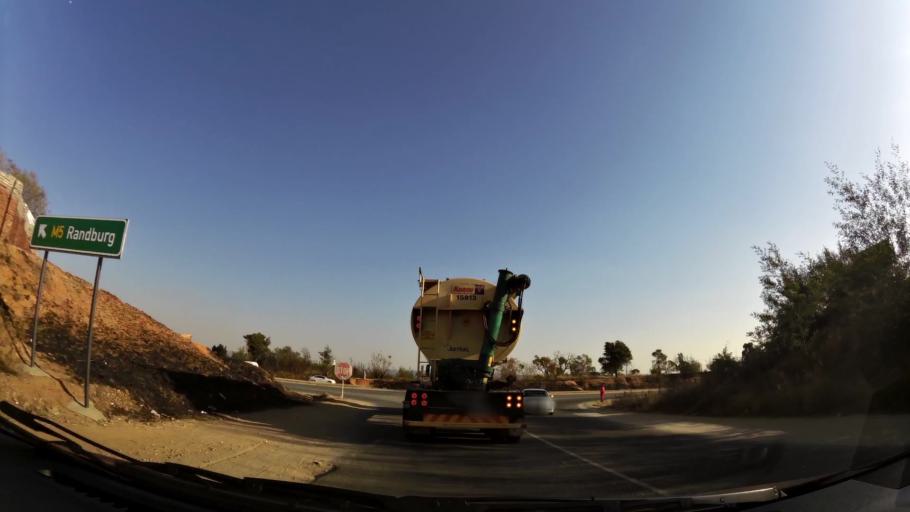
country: ZA
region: Gauteng
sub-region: West Rand District Municipality
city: Muldersdriseloop
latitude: -26.0270
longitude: 27.8681
